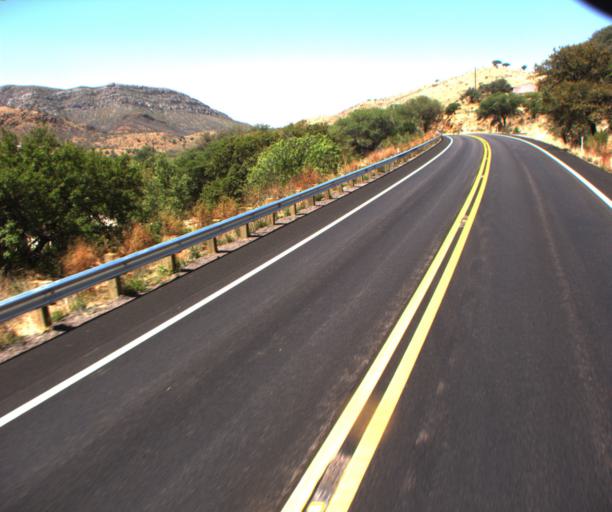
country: US
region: Arizona
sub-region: Cochise County
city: Bisbee
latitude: 31.4946
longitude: -109.9918
